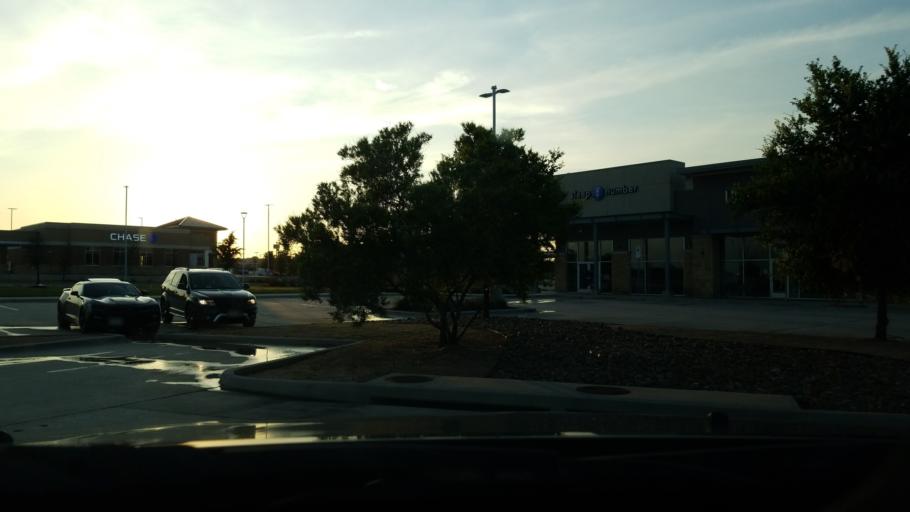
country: US
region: Texas
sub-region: Denton County
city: Denton
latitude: 33.2289
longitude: -97.1687
